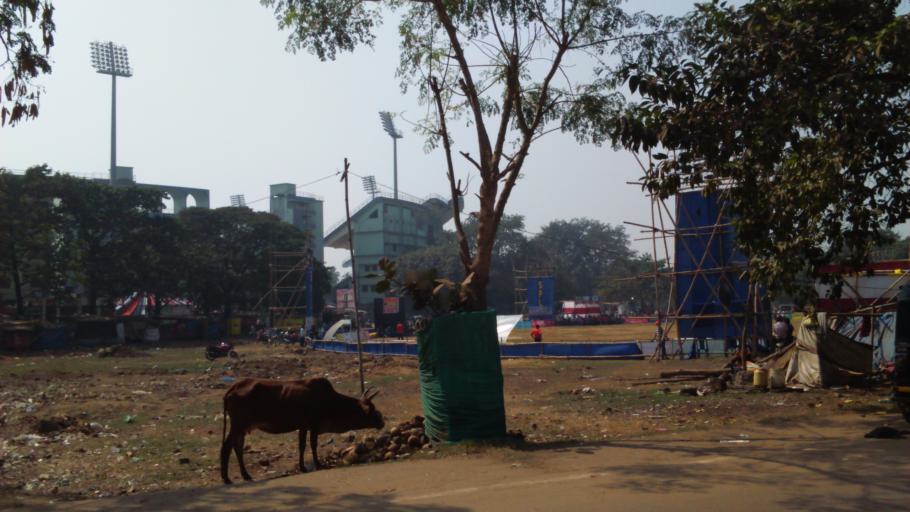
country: IN
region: Odisha
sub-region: Cuttack
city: Cuttack
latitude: 20.4832
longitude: 85.8694
